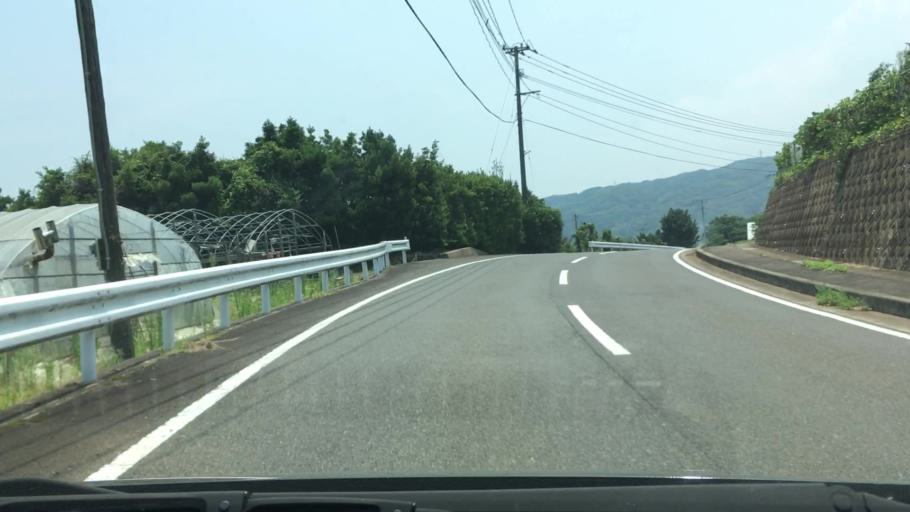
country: JP
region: Nagasaki
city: Sasebo
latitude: 33.0690
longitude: 129.6807
